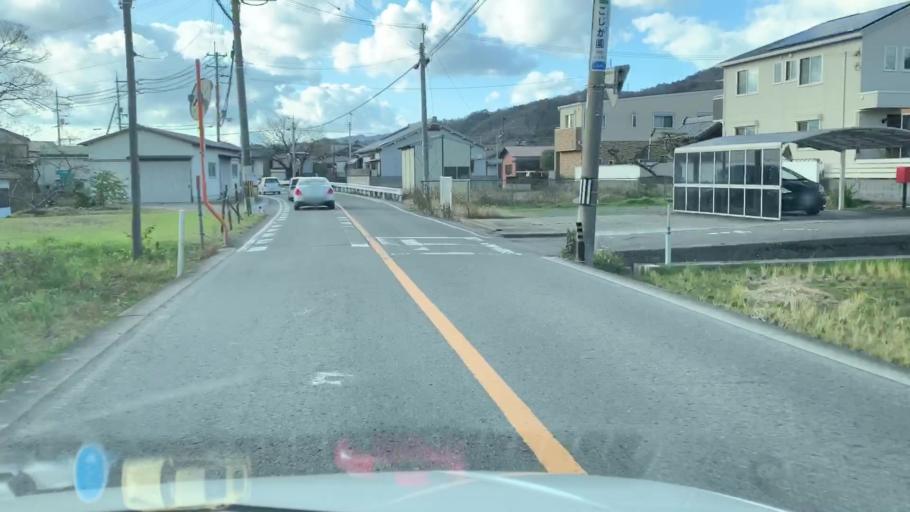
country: JP
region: Wakayama
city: Iwade
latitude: 34.2721
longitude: 135.2585
